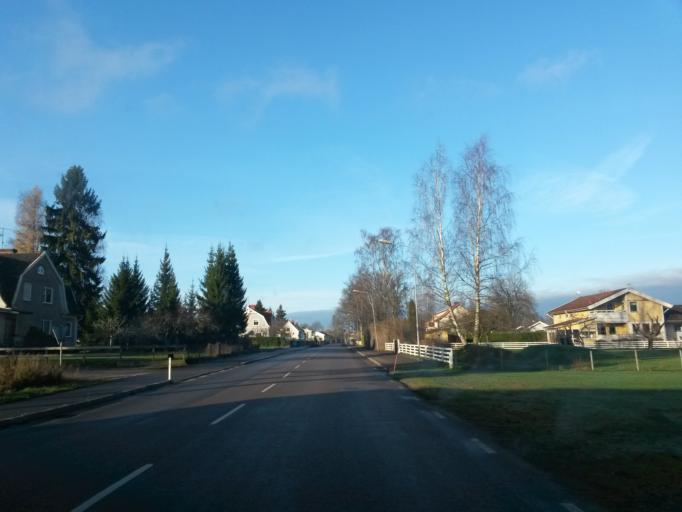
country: SE
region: Vaestra Goetaland
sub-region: Essunga Kommun
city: Nossebro
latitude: 58.1851
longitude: 12.7280
